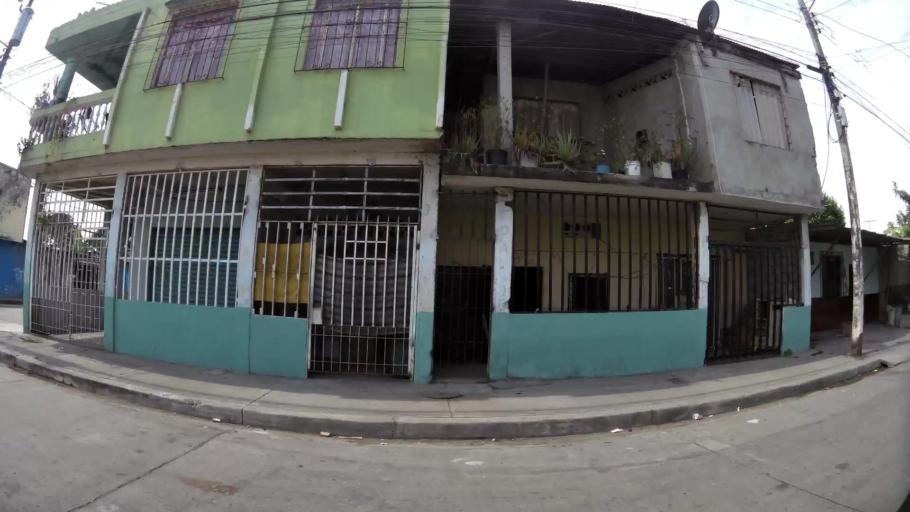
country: EC
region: Guayas
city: Guayaquil
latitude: -2.2796
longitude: -79.8874
